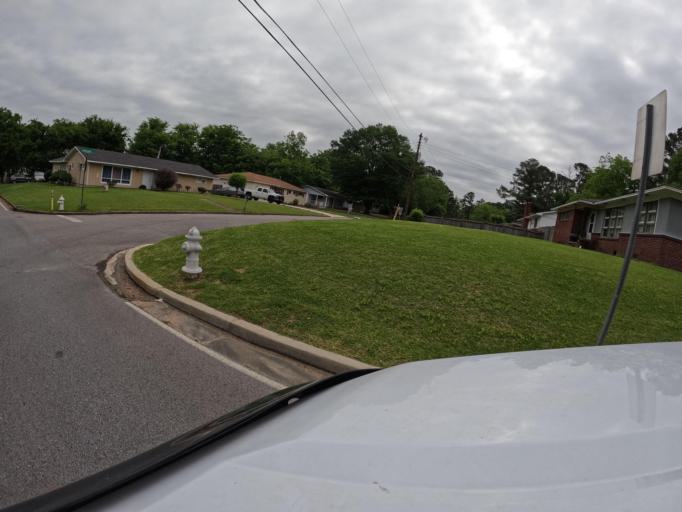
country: US
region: Mississippi
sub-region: Lee County
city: Tupelo
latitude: 34.2659
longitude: -88.7377
